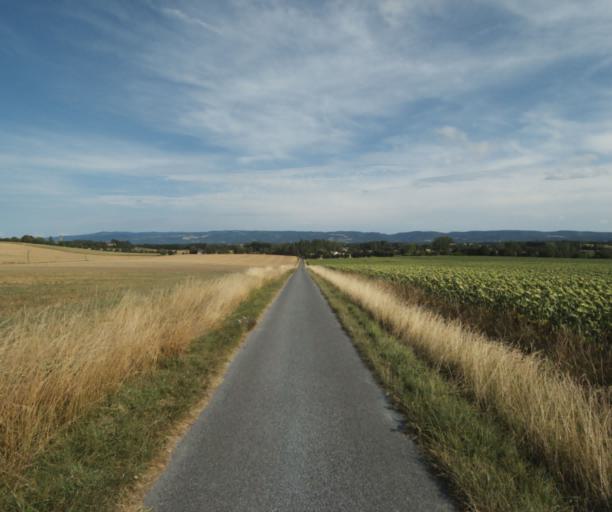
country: FR
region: Midi-Pyrenees
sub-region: Departement du Tarn
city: Puylaurens
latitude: 43.5293
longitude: 1.9931
